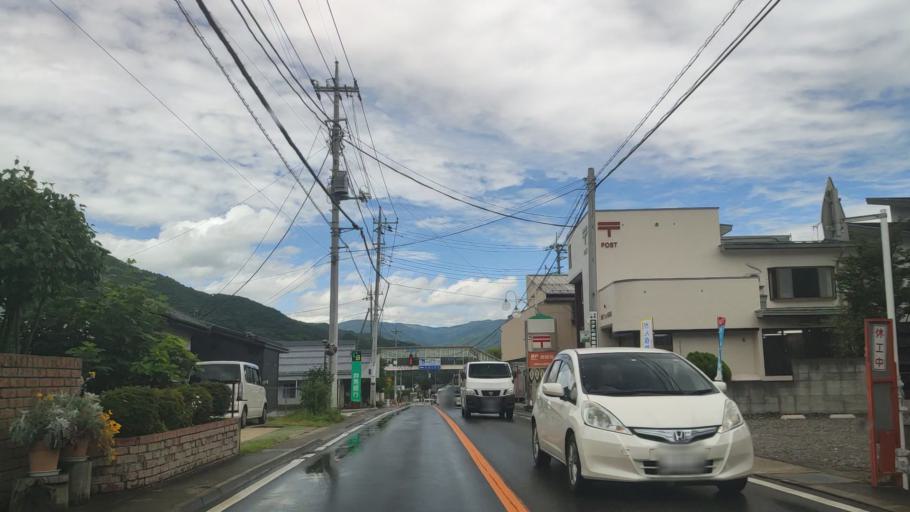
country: JP
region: Gunma
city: Numata
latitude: 36.7714
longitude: 139.2261
